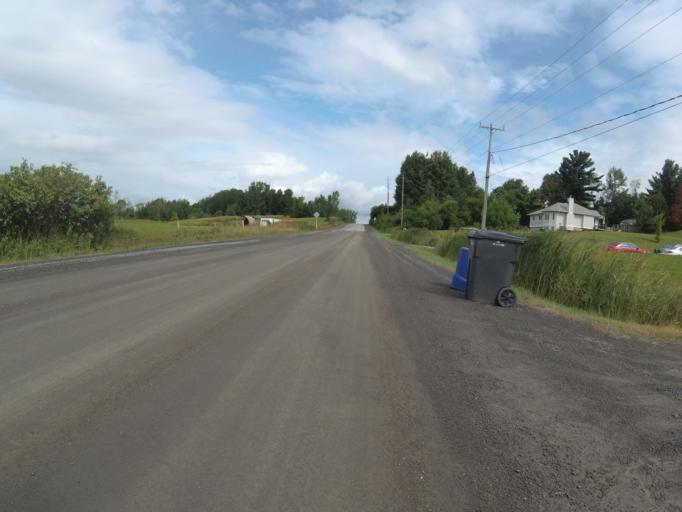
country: CA
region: Ontario
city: Clarence-Rockland
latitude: 45.4868
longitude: -75.3124
